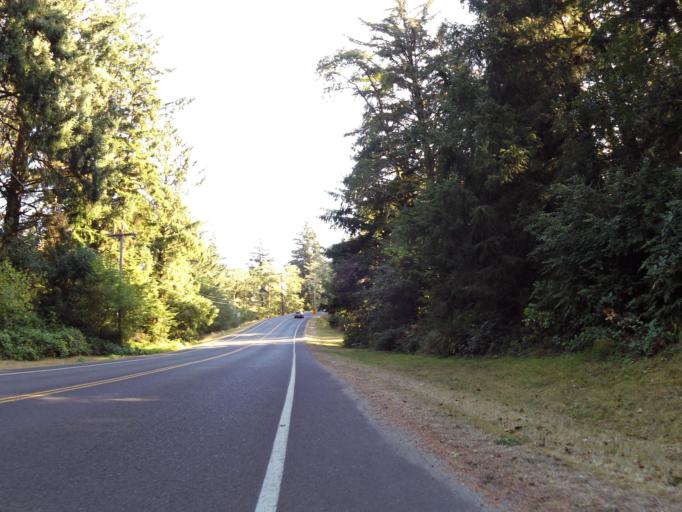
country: US
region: Oregon
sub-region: Clatsop County
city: Warrenton
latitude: 46.1835
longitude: -123.9592
